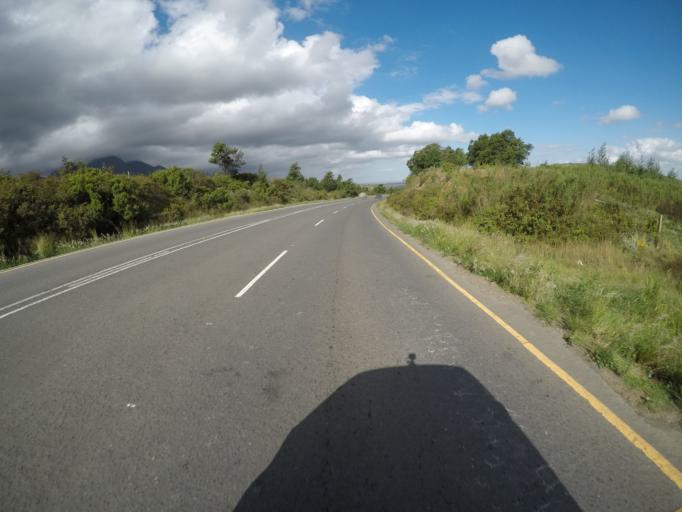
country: ZA
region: Western Cape
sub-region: Overberg District Municipality
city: Swellendam
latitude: -33.9936
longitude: 20.3512
